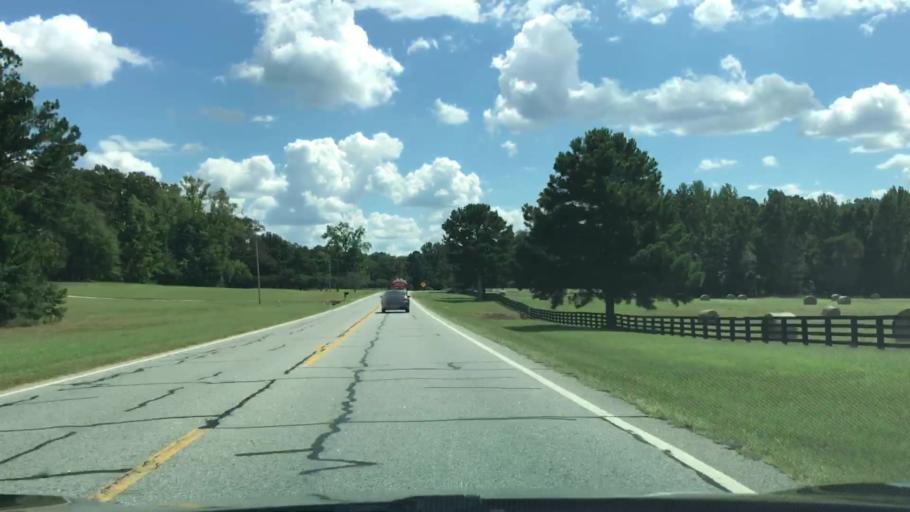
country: US
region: Georgia
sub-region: Oconee County
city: Watkinsville
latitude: 33.7539
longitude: -83.3038
